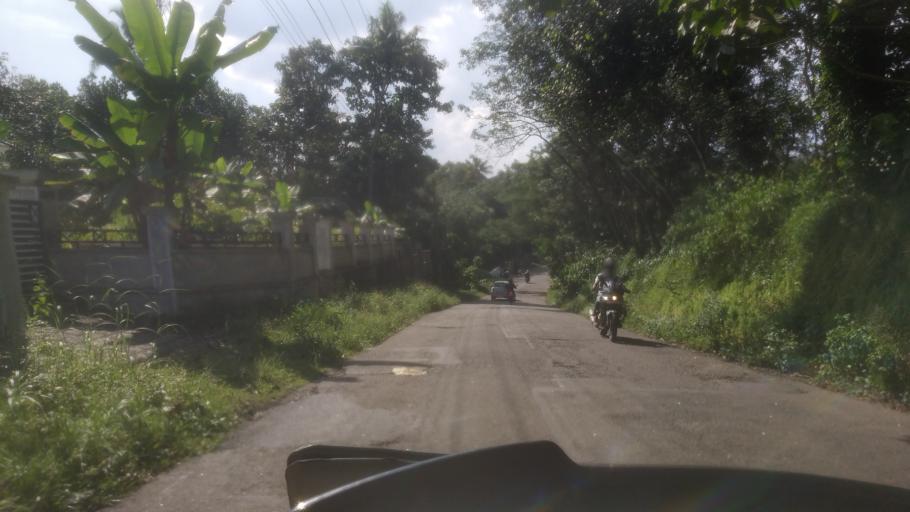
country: IN
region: Kerala
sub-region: Ernakulam
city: Kotamangalam
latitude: 10.0040
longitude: 76.6968
